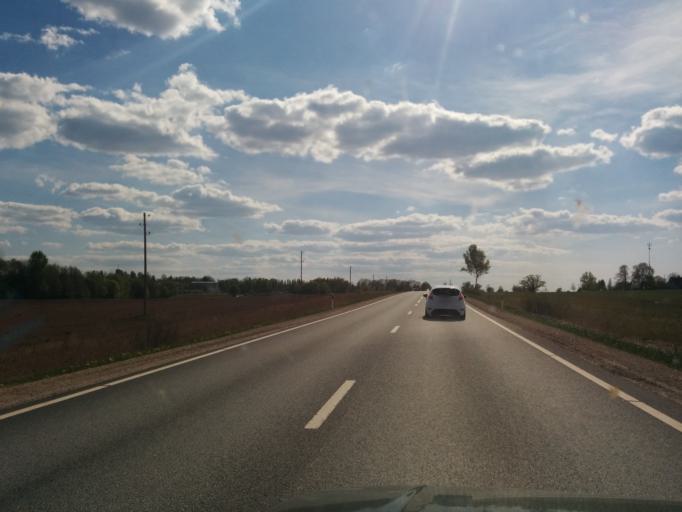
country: LV
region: Sigulda
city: Sigulda
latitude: 57.2674
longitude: 24.8834
